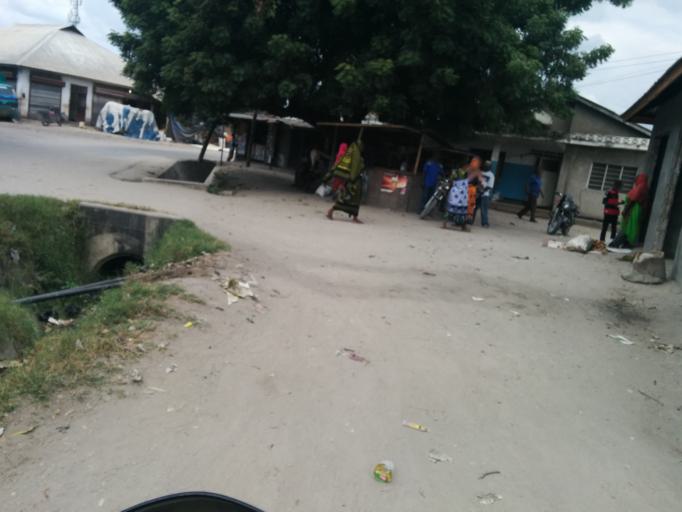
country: TZ
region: Dar es Salaam
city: Dar es Salaam
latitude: -6.8656
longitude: 39.2497
